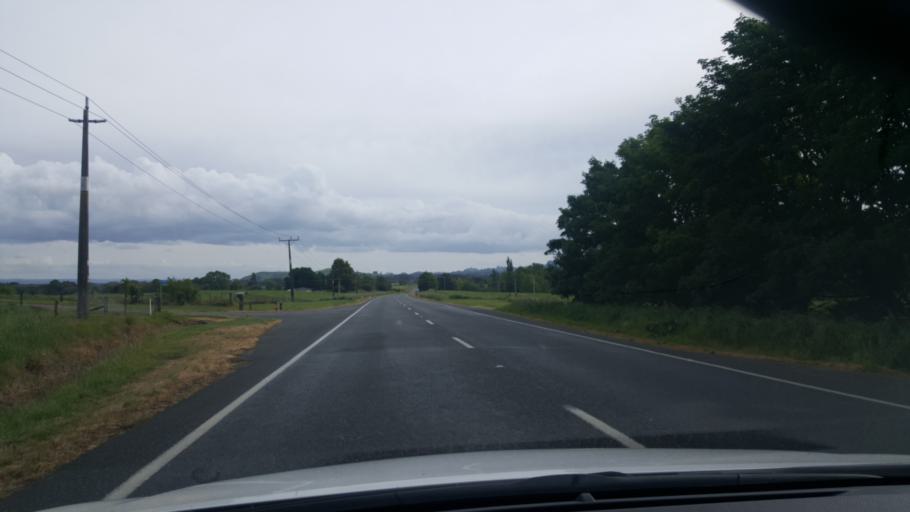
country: NZ
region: Bay of Plenty
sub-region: Rotorua District
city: Rotorua
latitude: -38.3956
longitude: 176.3361
